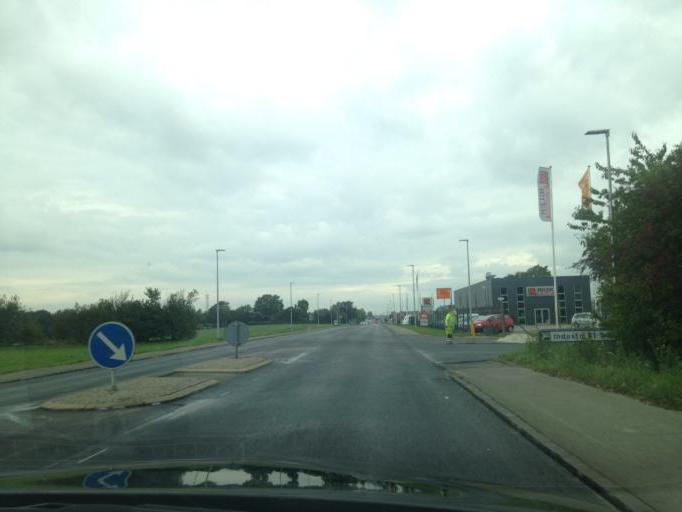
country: DK
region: South Denmark
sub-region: Kolding Kommune
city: Kolding
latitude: 55.4613
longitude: 9.4733
